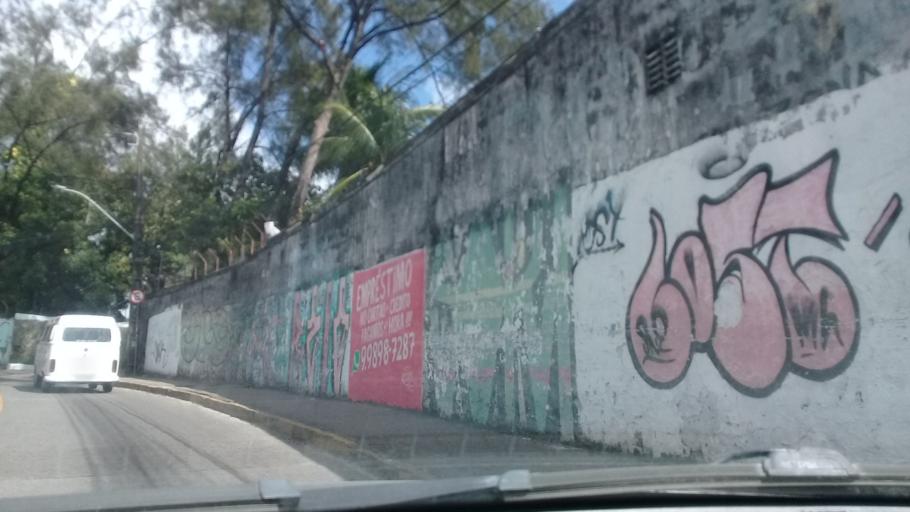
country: BR
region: Pernambuco
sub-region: Jaboatao Dos Guararapes
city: Jaboatao dos Guararapes
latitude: -8.1184
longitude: -34.9445
